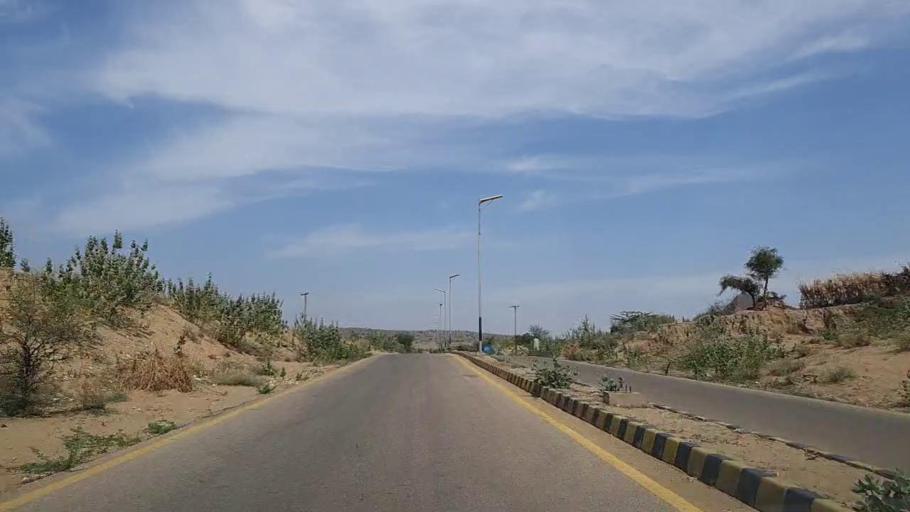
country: PK
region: Sindh
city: Mithi
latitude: 24.7591
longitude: 69.7963
